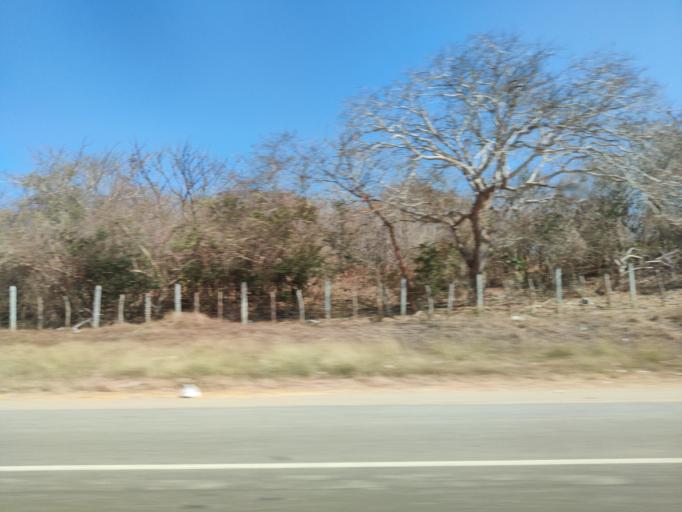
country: CO
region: Atlantico
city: Puerto Colombia
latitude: 10.9678
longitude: -74.9808
